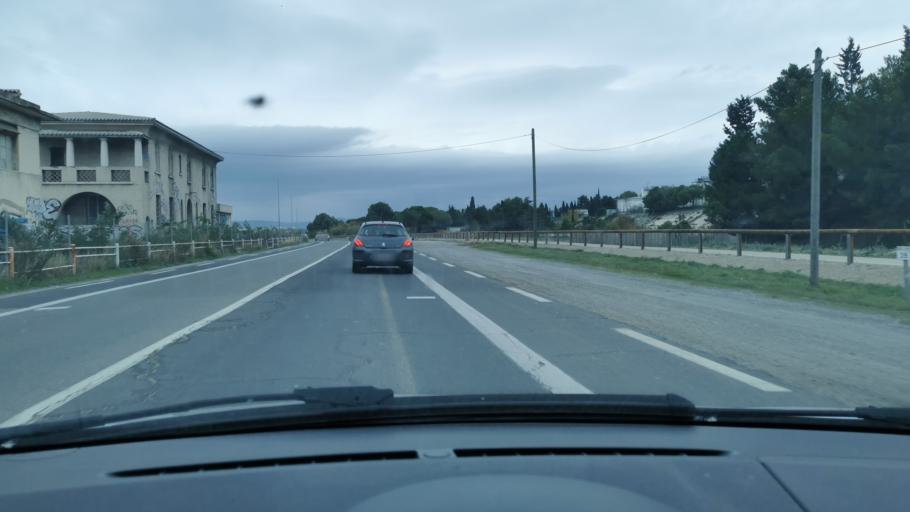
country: FR
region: Languedoc-Roussillon
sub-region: Departement de l'Herault
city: Sete
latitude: 43.4293
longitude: 3.7055
